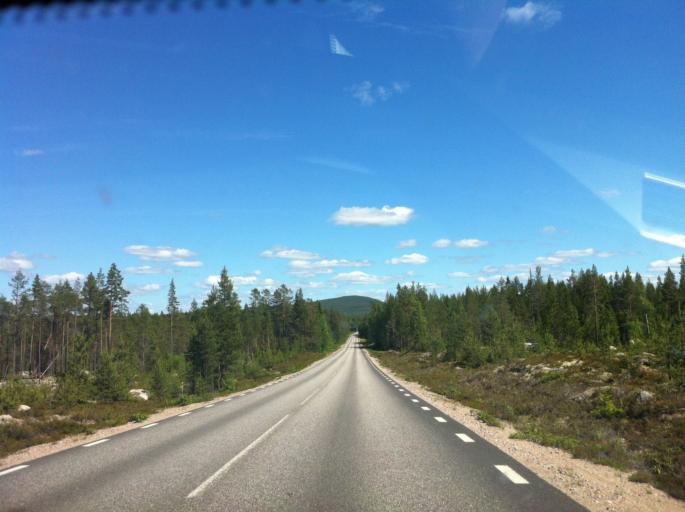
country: SE
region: Jaemtland
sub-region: Harjedalens Kommun
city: Sveg
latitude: 61.9961
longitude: 14.9864
